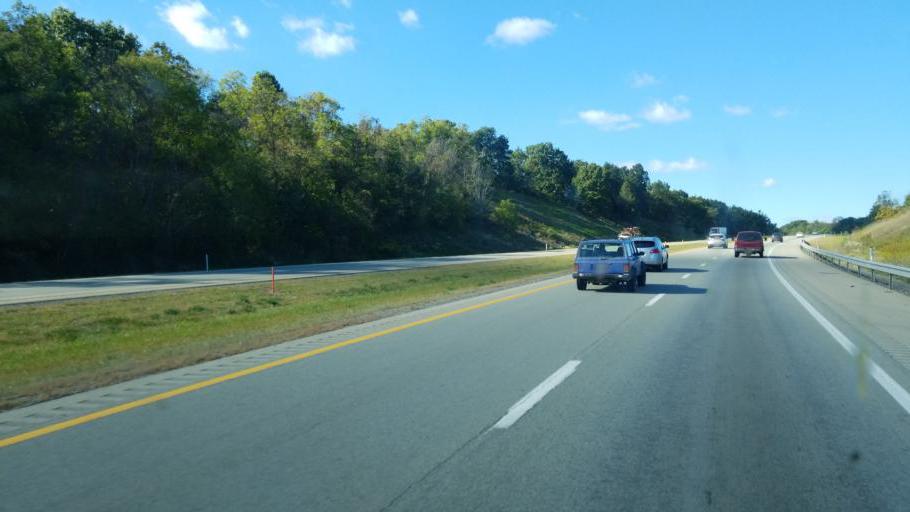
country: US
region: Pennsylvania
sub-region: Greene County
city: Morrisville
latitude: 39.8332
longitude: -80.1114
